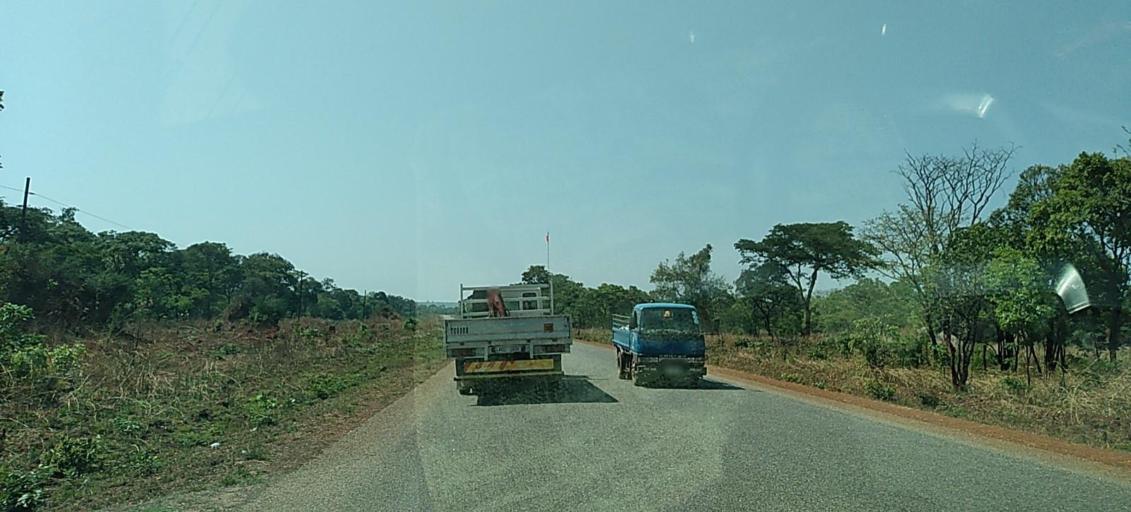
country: ZM
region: North-Western
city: Solwezi
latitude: -12.2111
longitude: 25.5593
